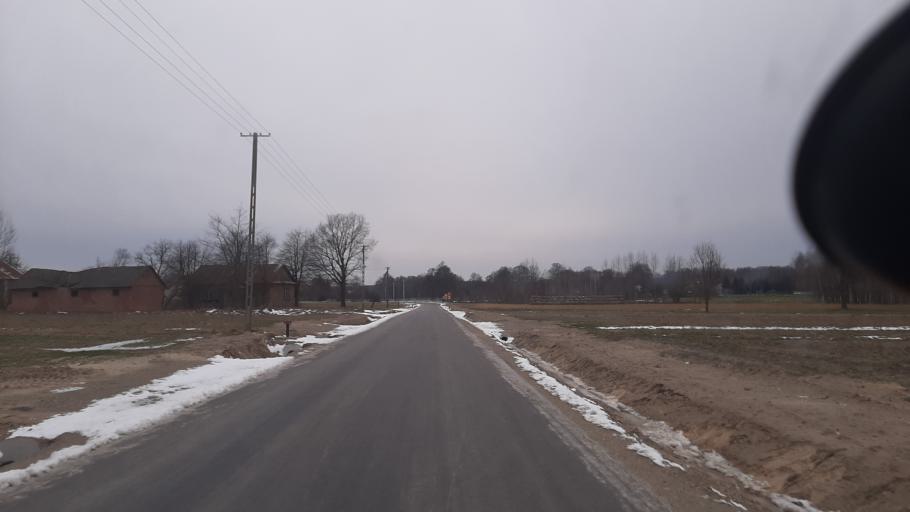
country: PL
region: Lublin Voivodeship
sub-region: Powiat lubartowski
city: Kamionka
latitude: 51.5126
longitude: 22.4637
